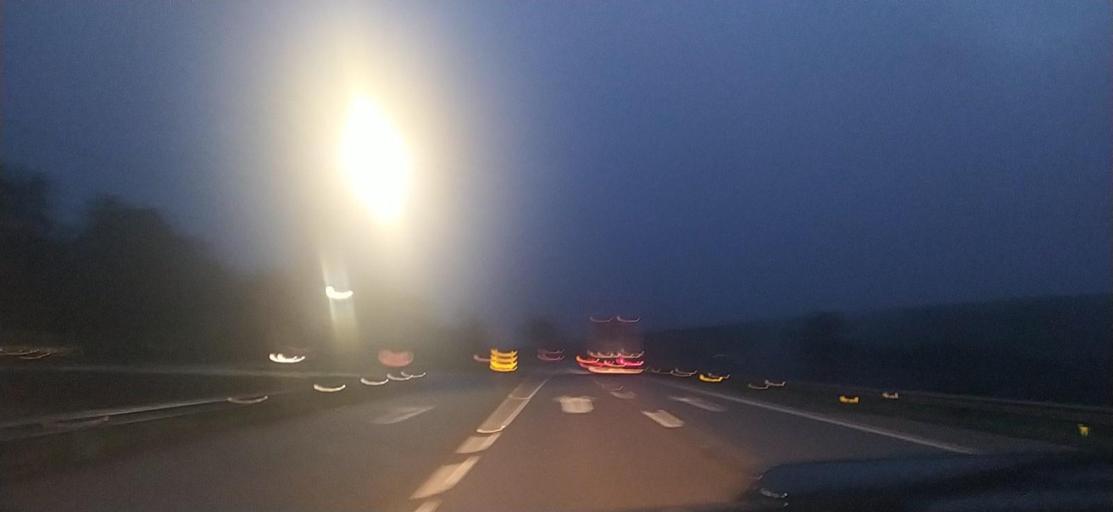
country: BR
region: Minas Gerais
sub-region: Sao Goncalo Do Sapucai
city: Sao Goncalo do Sapucai
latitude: -21.9323
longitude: -45.6120
